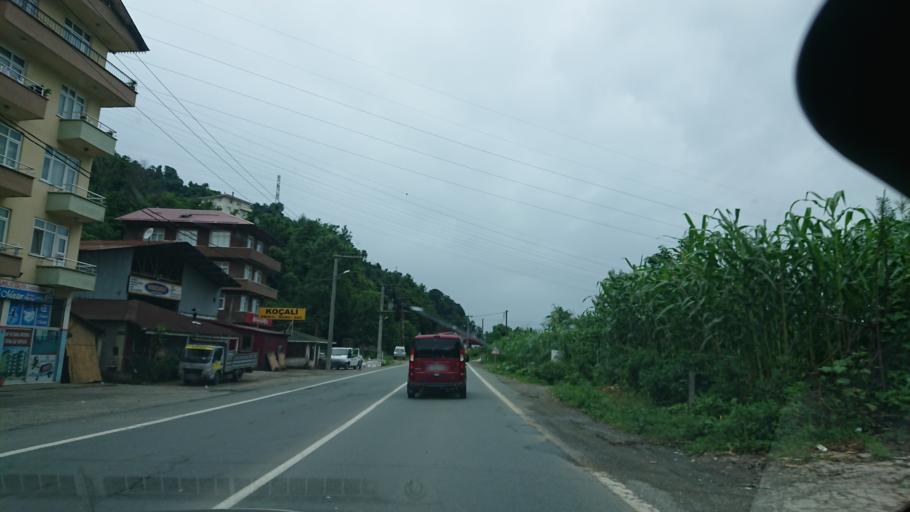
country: TR
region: Rize
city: Gundogdu
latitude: 41.0321
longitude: 40.5821
